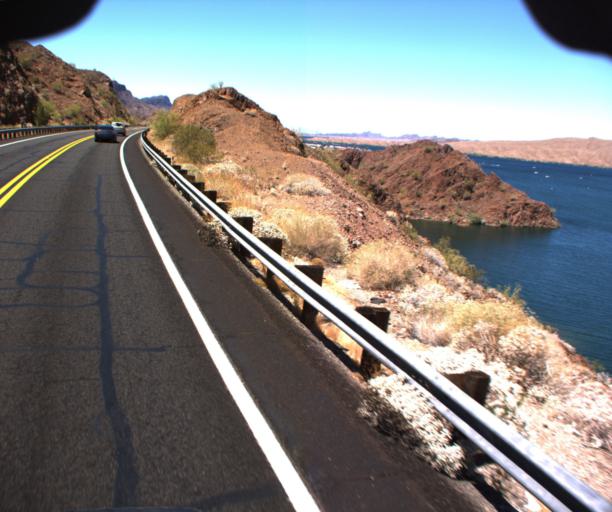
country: US
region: Arizona
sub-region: La Paz County
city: Cienega Springs
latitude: 34.2891
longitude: -114.1113
